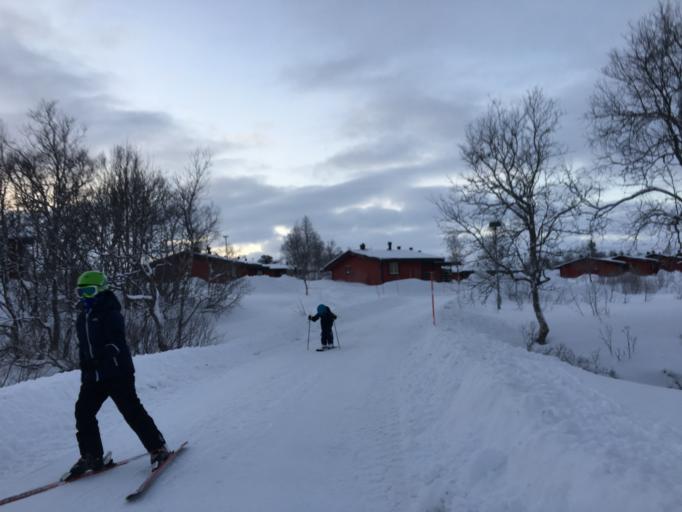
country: NO
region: Nord-Trondelag
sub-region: Meraker
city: Meraker
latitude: 63.3204
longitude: 12.0871
